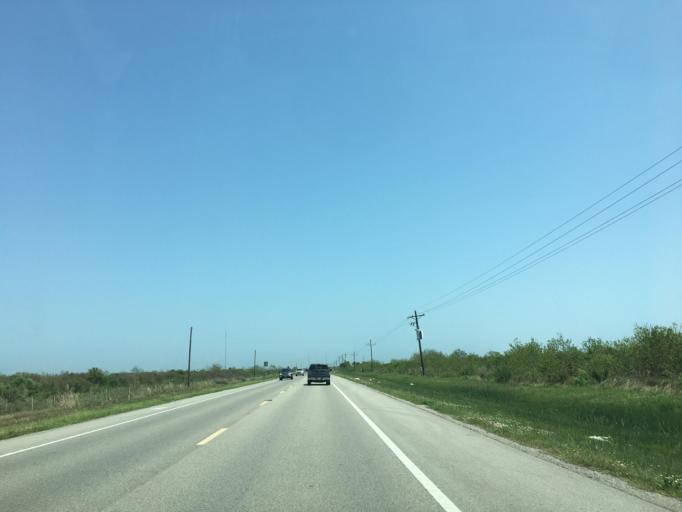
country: US
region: Texas
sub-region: Galveston County
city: Galveston
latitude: 29.4044
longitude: -94.7214
